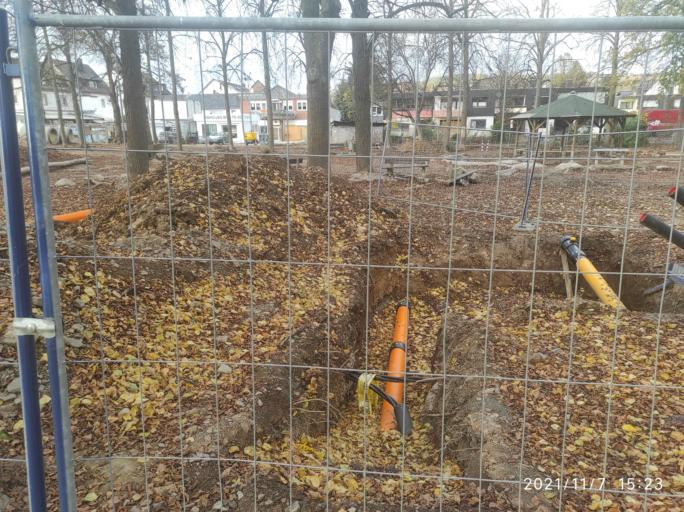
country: DE
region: Rheinland-Pfalz
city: Bad Neuenahr-Ahrweiler
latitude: 50.5430
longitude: 7.1249
